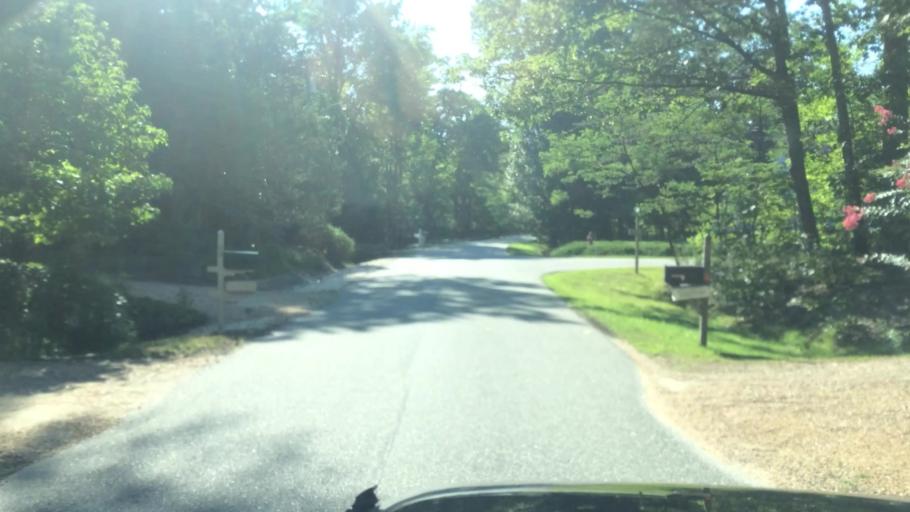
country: US
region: Virginia
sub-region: James City County
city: Williamsburg
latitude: 37.2368
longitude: -76.8022
